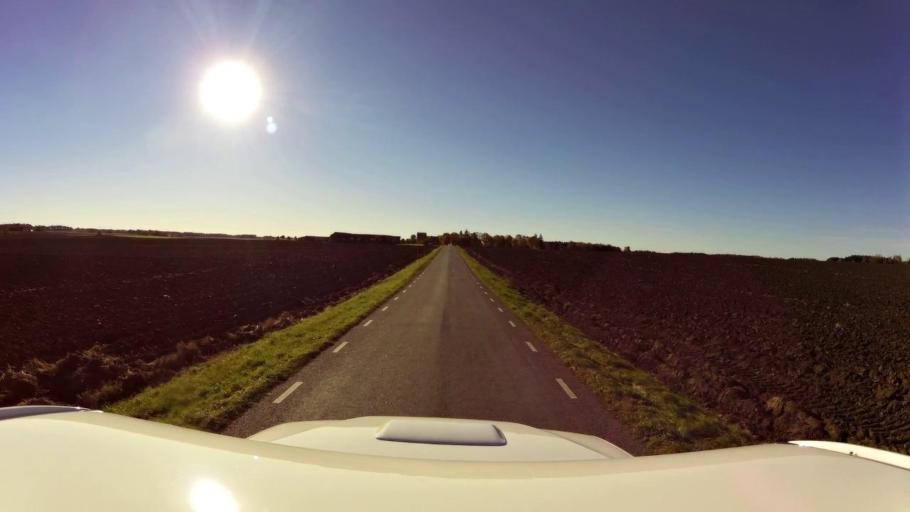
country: SE
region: OEstergoetland
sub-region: Linkopings Kommun
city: Ljungsbro
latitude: 58.5153
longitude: 15.4184
